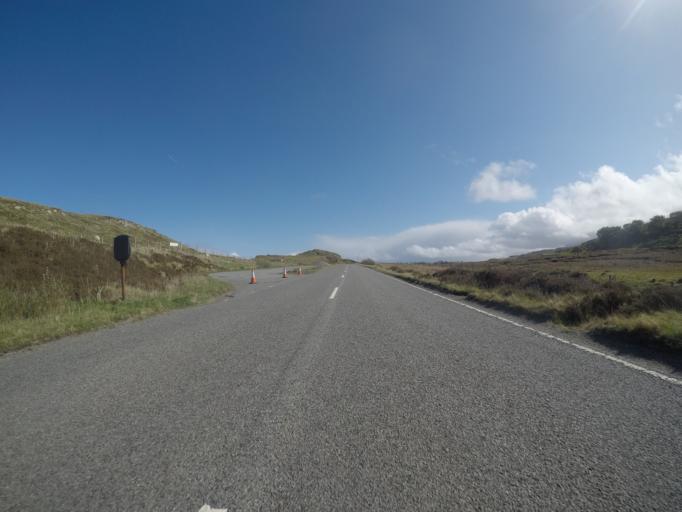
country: GB
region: Scotland
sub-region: Highland
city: Portree
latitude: 57.6028
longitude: -6.1679
